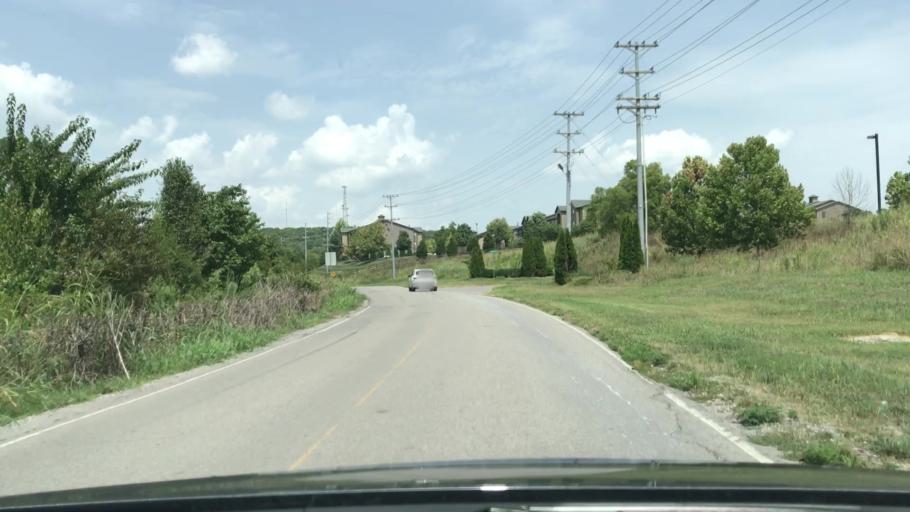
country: US
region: Tennessee
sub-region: Rutherford County
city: La Vergne
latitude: 35.9731
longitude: -86.5795
